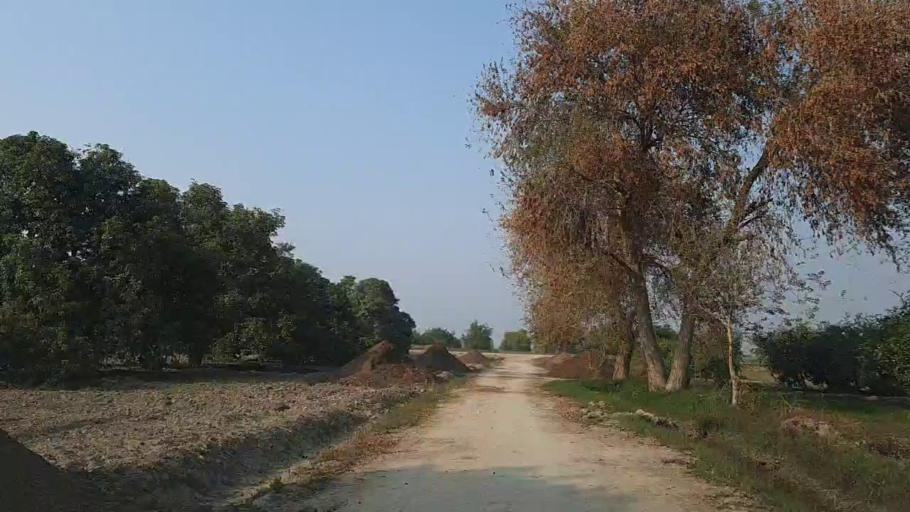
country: PK
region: Sindh
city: Sann
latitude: 26.1111
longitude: 68.1615
